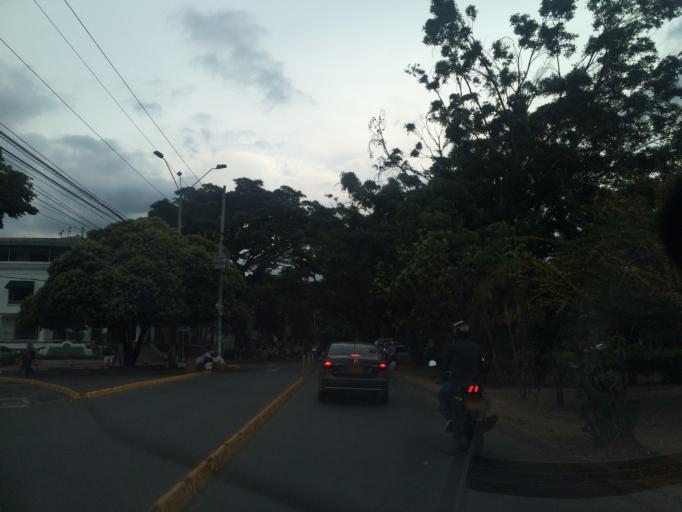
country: CO
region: Valle del Cauca
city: Cali
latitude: 3.3640
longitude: -76.5327
